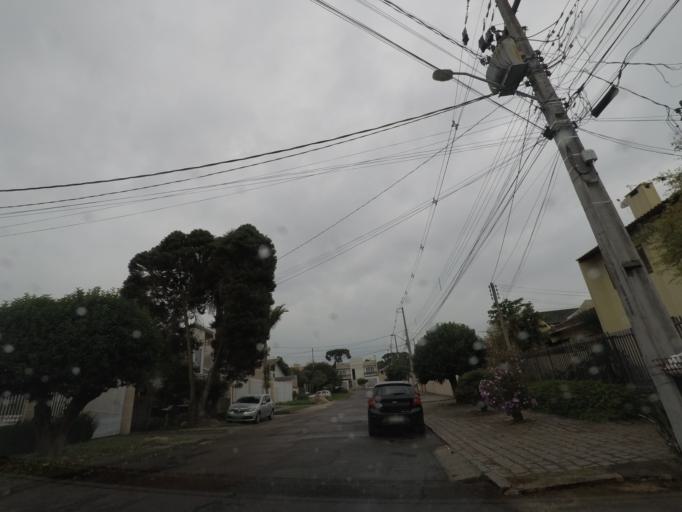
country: BR
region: Parana
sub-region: Curitiba
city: Curitiba
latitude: -25.4755
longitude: -49.3102
